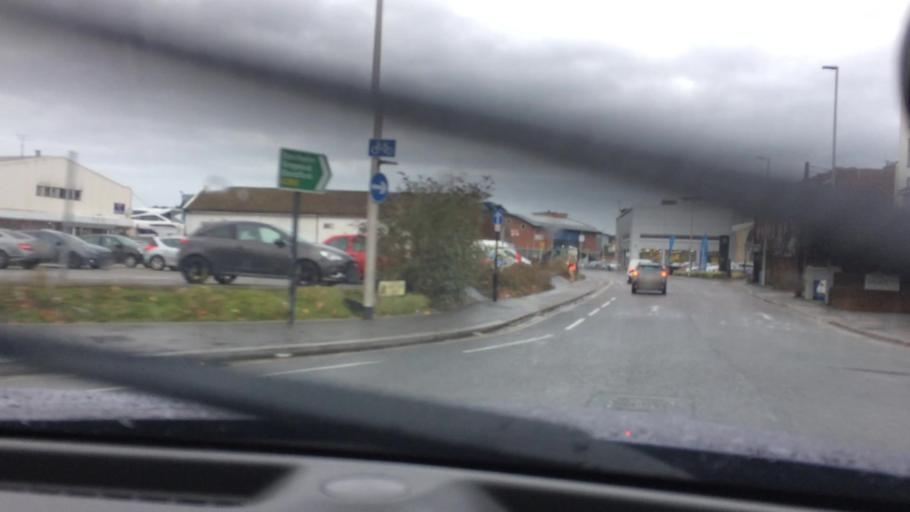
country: GB
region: England
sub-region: Poole
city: Poole
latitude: 50.7147
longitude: -1.9908
